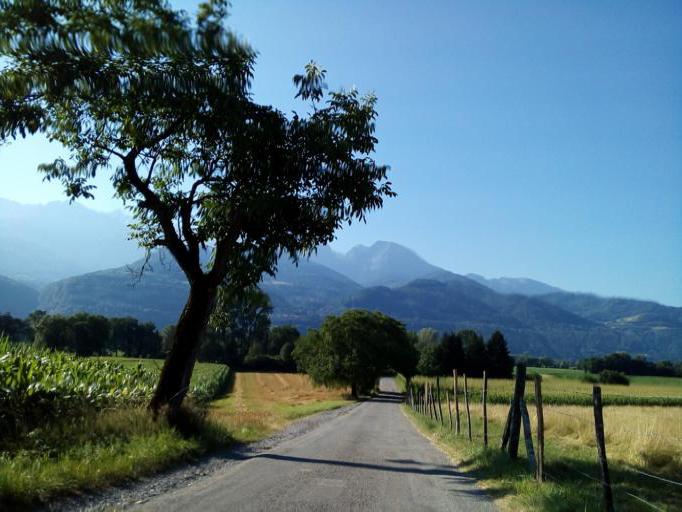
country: FR
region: Rhone-Alpes
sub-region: Departement de l'Isere
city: Bernin
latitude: 45.2577
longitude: 5.8700
